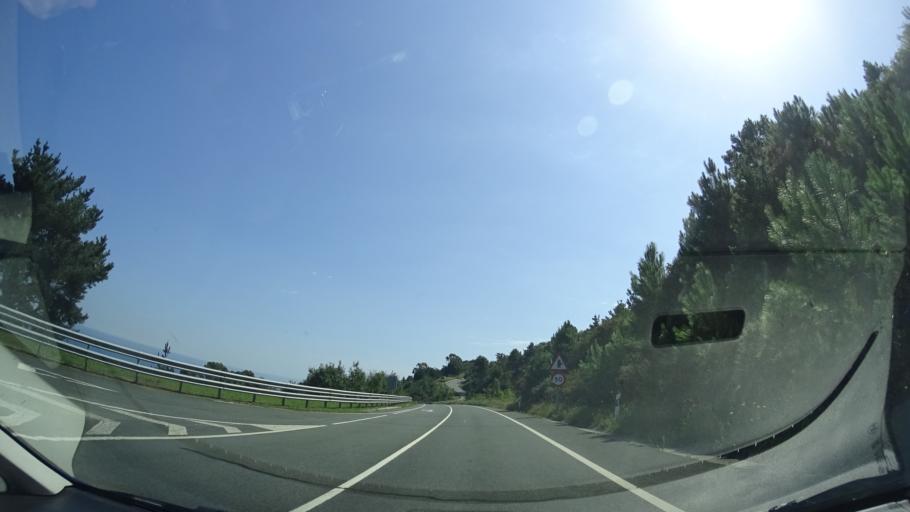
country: ES
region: Basque Country
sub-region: Bizkaia
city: Bakio
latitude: 43.4406
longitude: -2.7700
